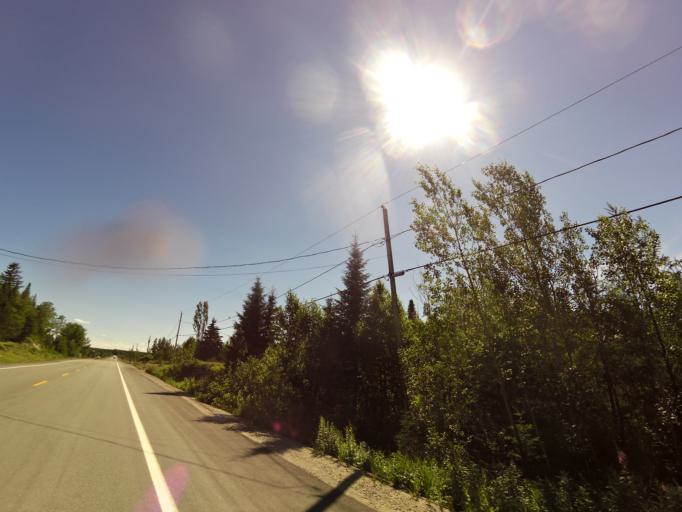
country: CA
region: Quebec
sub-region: Abitibi-Temiscamingue
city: Senneterre
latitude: 48.2113
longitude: -77.3546
